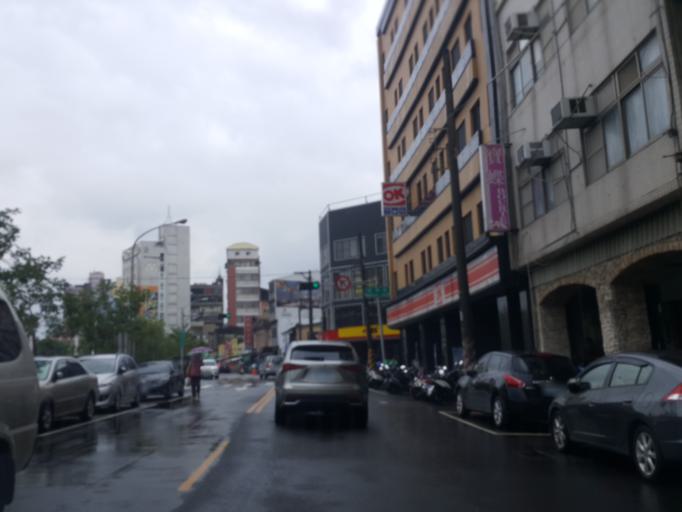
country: TW
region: Taiwan
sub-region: Taichung City
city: Taichung
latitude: 24.1416
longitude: 120.6767
